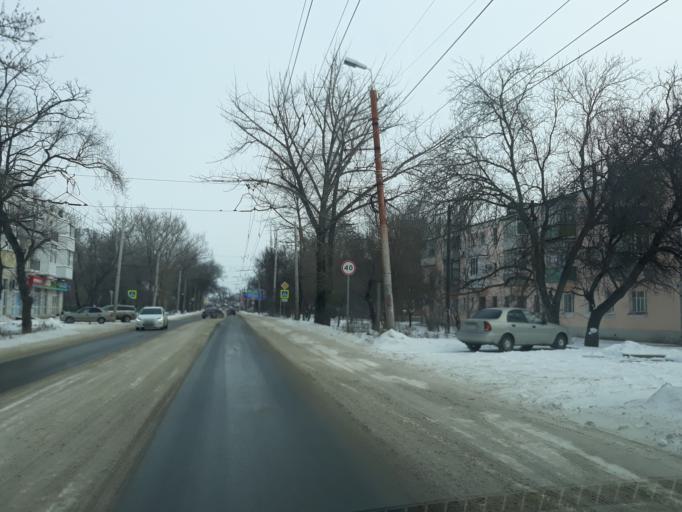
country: RU
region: Rostov
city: Taganrog
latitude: 47.2227
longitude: 38.8787
